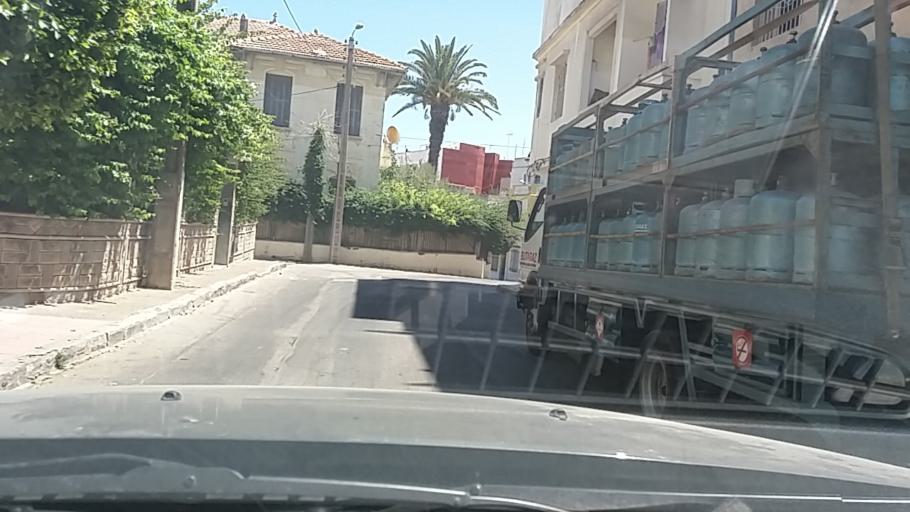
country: MA
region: Tanger-Tetouan
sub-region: Tanger-Assilah
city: Tangier
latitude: 35.7882
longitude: -5.8176
